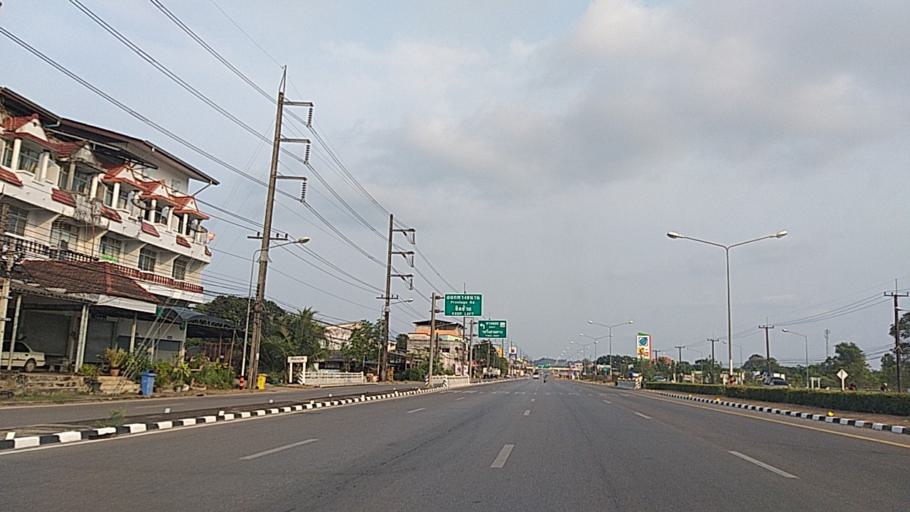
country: TH
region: Trat
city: Khao Saming
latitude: 12.3810
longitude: 102.3743
